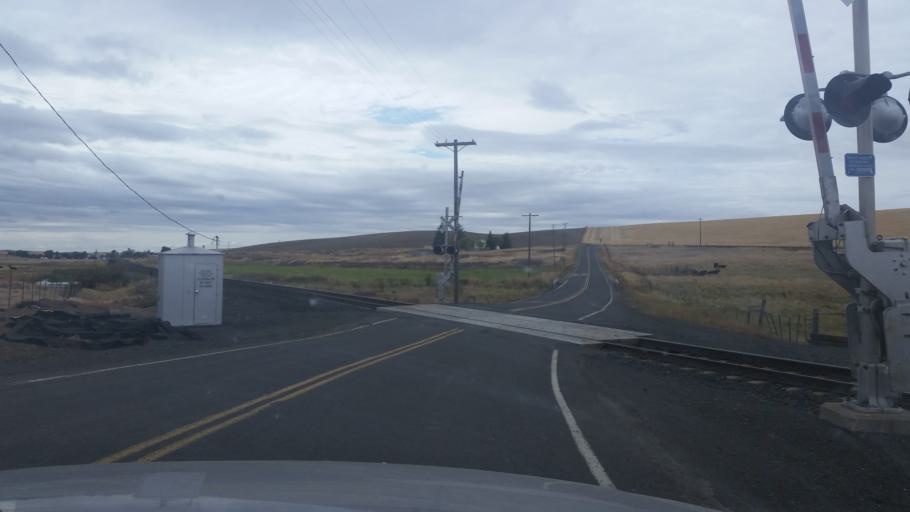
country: US
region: Washington
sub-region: Spokane County
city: Medical Lake
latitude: 47.5215
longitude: -117.9194
